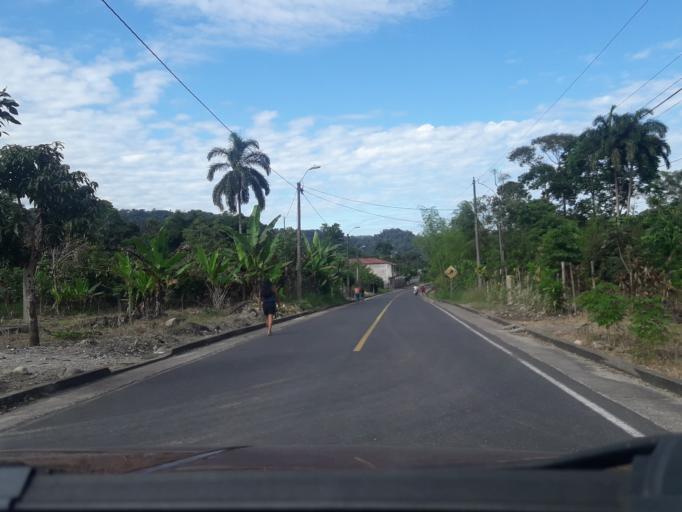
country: EC
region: Napo
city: Tena
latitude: -0.9793
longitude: -77.8430
